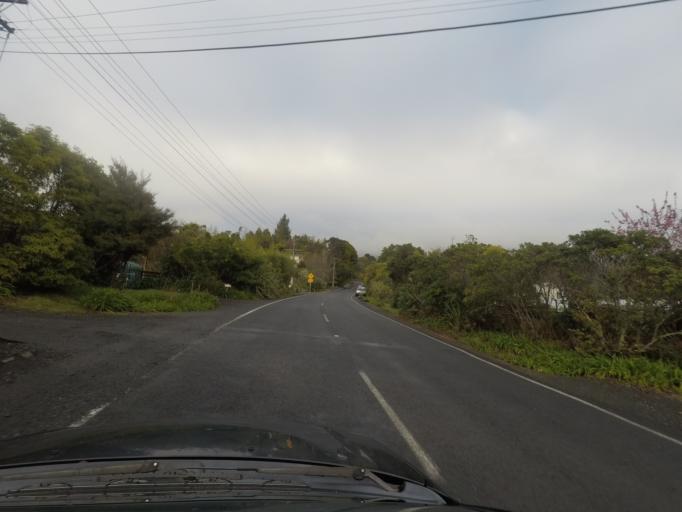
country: NZ
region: Auckland
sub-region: Auckland
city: Waitakere
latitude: -36.9201
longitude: 174.5857
